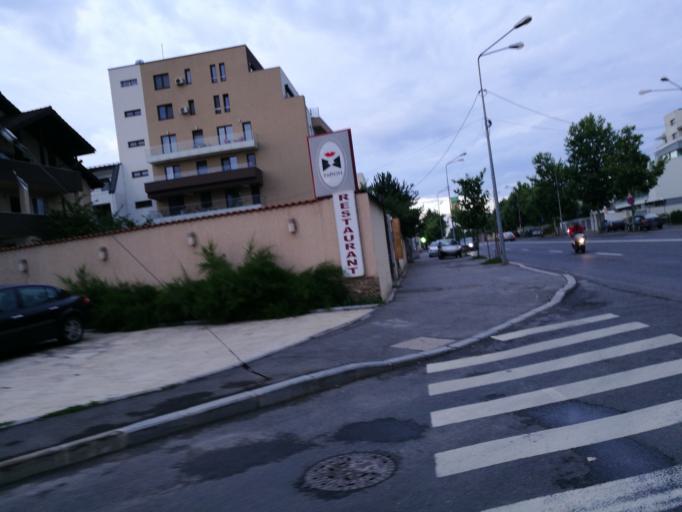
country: RO
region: Ilfov
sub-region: Comuna Otopeni
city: Otopeni
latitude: 44.5032
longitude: 26.0516
